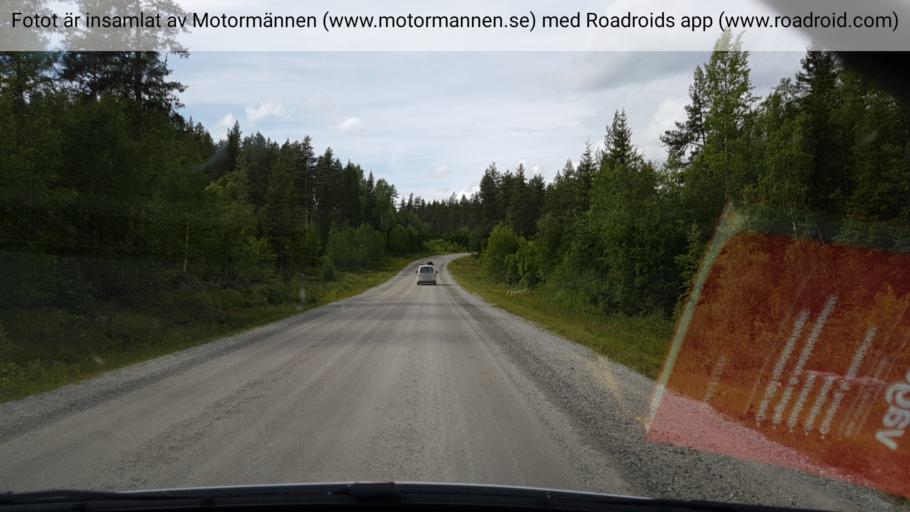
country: SE
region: Vaesternorrland
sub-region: Solleftea Kommun
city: Solleftea
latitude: 63.3134
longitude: 17.2549
